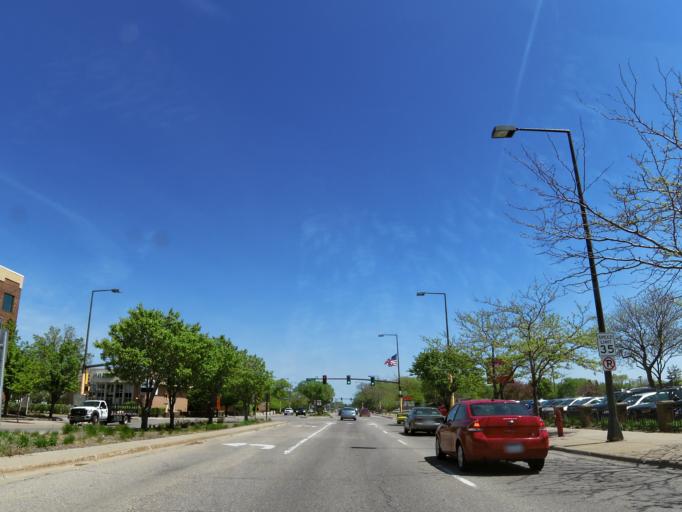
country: US
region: Minnesota
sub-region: Hennepin County
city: Bloomington
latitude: 44.8263
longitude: -93.2878
